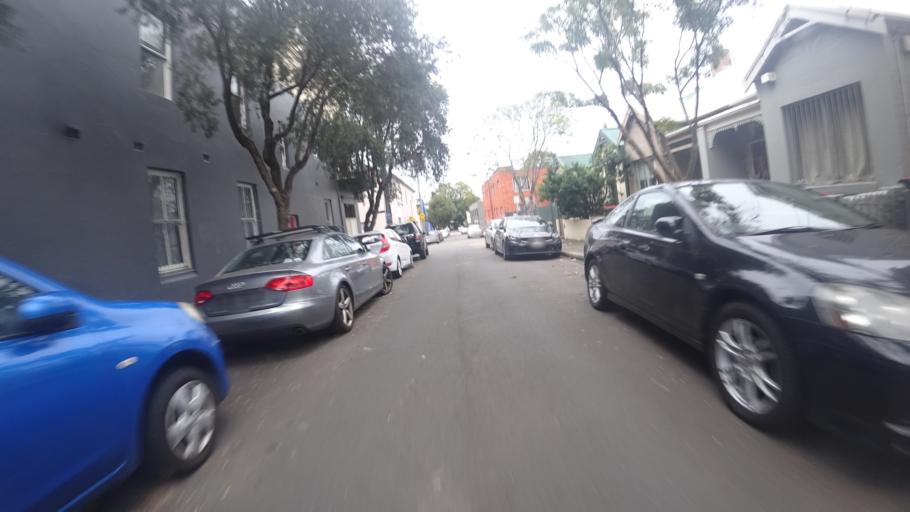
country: AU
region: New South Wales
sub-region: Marrickville
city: Newtown
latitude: -33.9067
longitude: 151.1775
